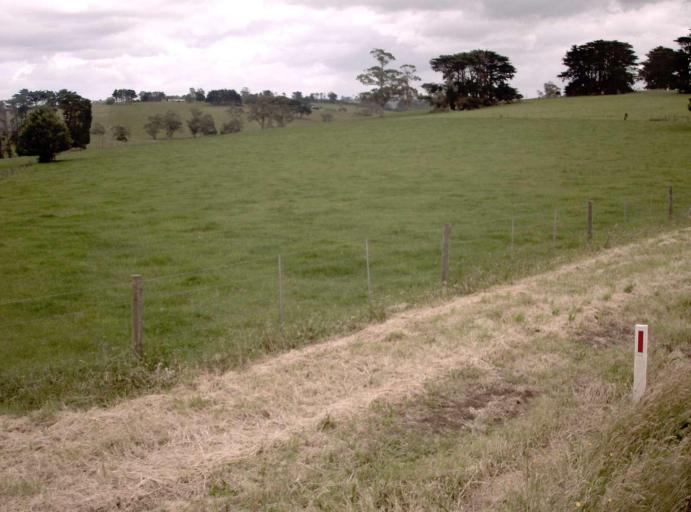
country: AU
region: Victoria
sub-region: Baw Baw
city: Warragul
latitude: -38.1264
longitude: 145.9857
